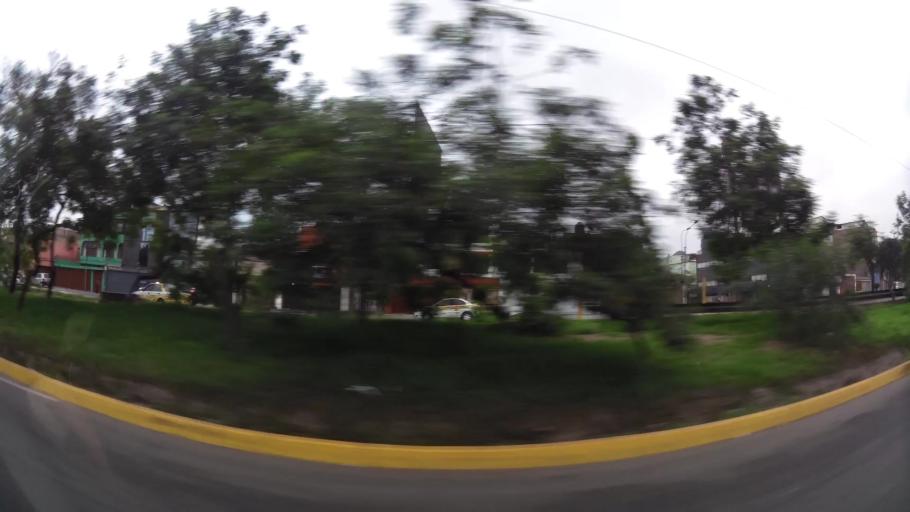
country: PE
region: Lima
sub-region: Lima
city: San Luis
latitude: -12.0855
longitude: -76.9867
